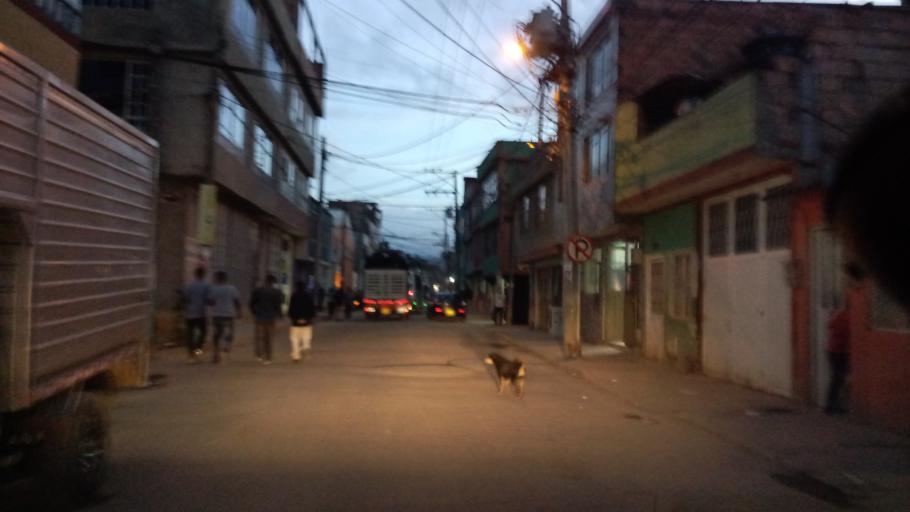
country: CO
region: Cundinamarca
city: Soacha
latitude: 4.5731
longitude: -74.2329
